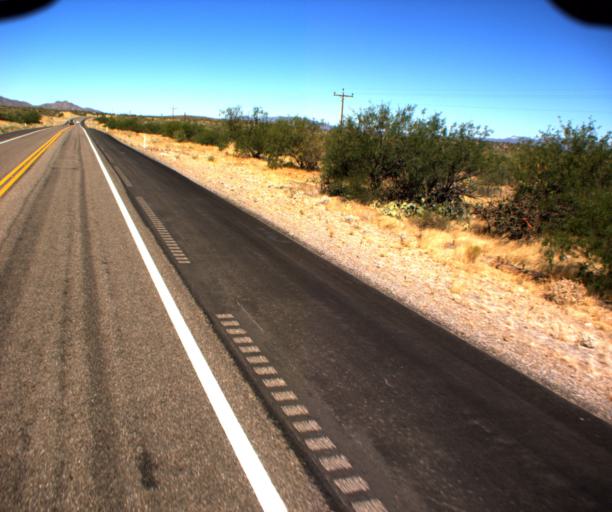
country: US
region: Arizona
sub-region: Pima County
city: Three Points
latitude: 32.0310
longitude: -111.5595
